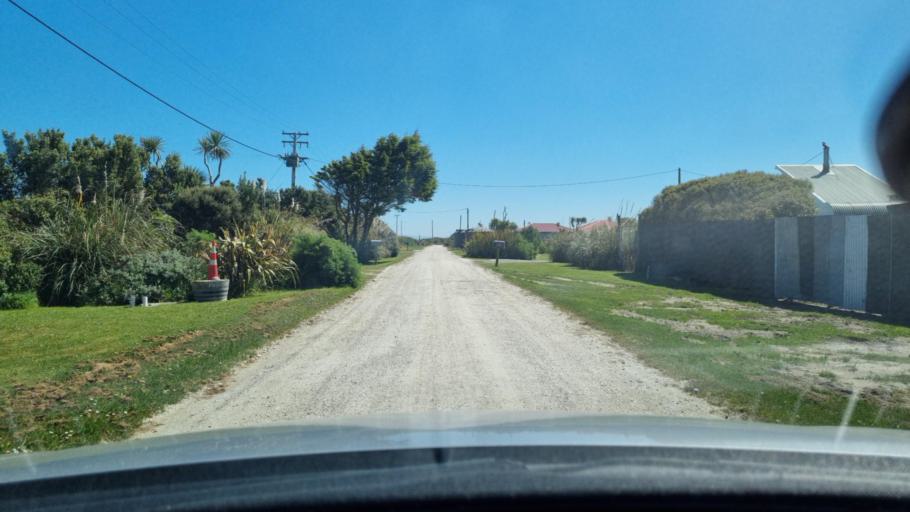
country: NZ
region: Southland
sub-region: Invercargill City
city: Invercargill
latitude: -46.4309
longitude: 168.2331
